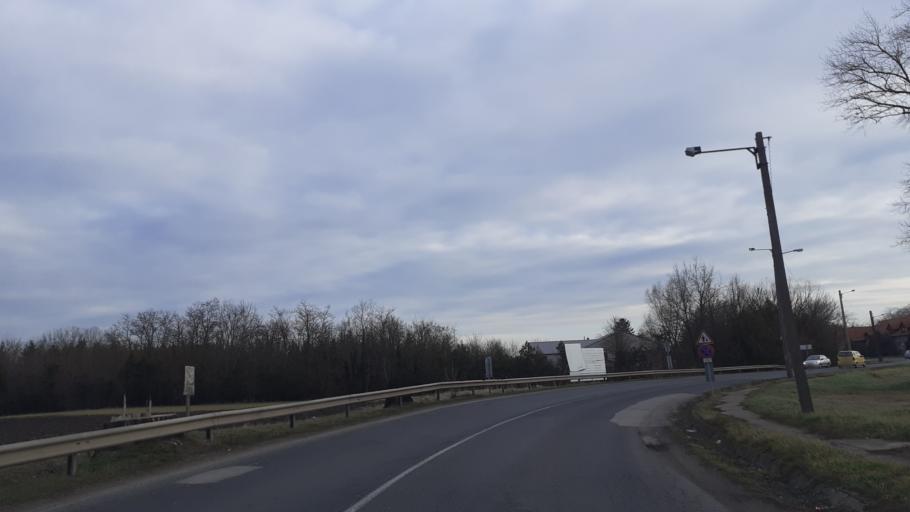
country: HU
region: Fejer
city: Sarbogard
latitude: 46.9001
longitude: 18.6135
